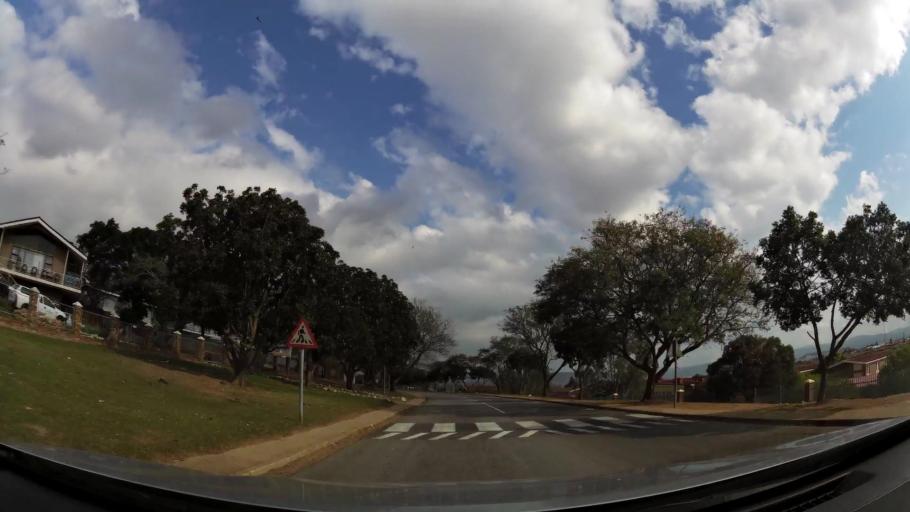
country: ZA
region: Eastern Cape
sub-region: Nelson Mandela Bay Metropolitan Municipality
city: Uitenhage
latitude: -33.7379
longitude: 25.4049
